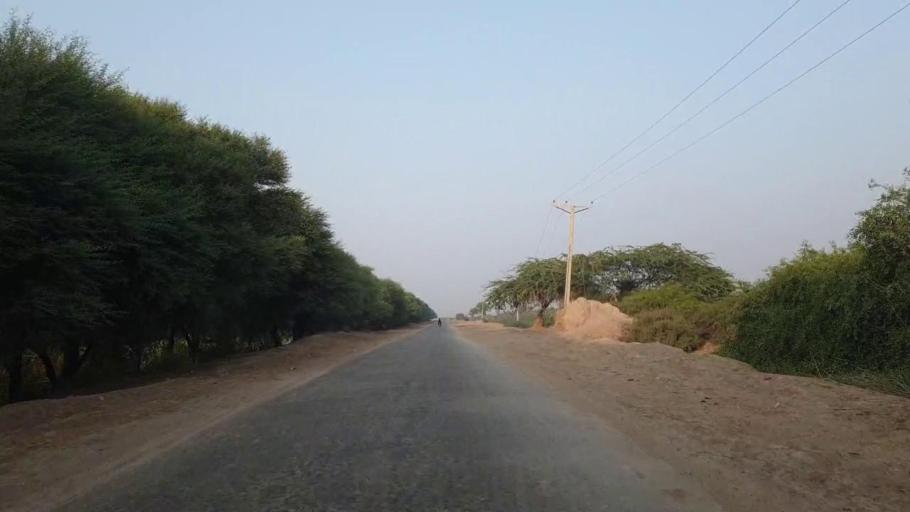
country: PK
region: Sindh
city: Tando Muhammad Khan
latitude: 25.1277
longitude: 68.4323
